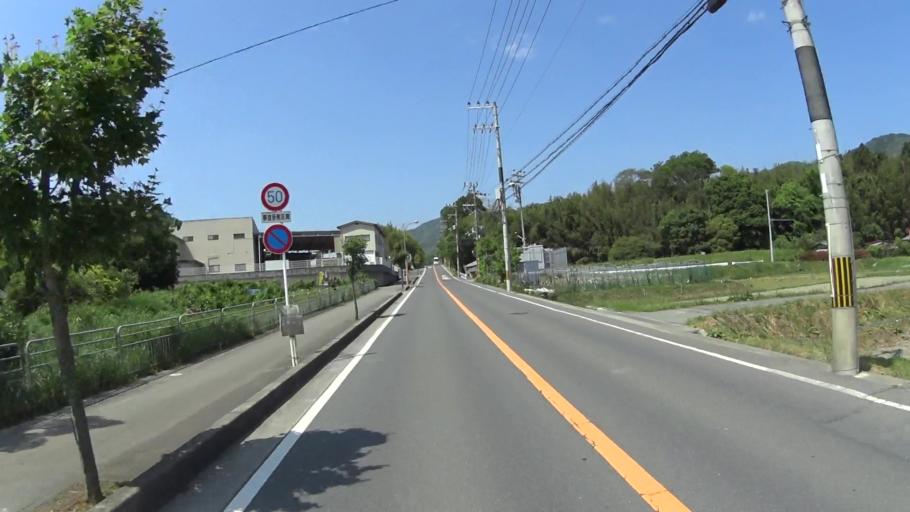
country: JP
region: Kyoto
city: Kameoka
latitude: 35.0406
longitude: 135.5752
